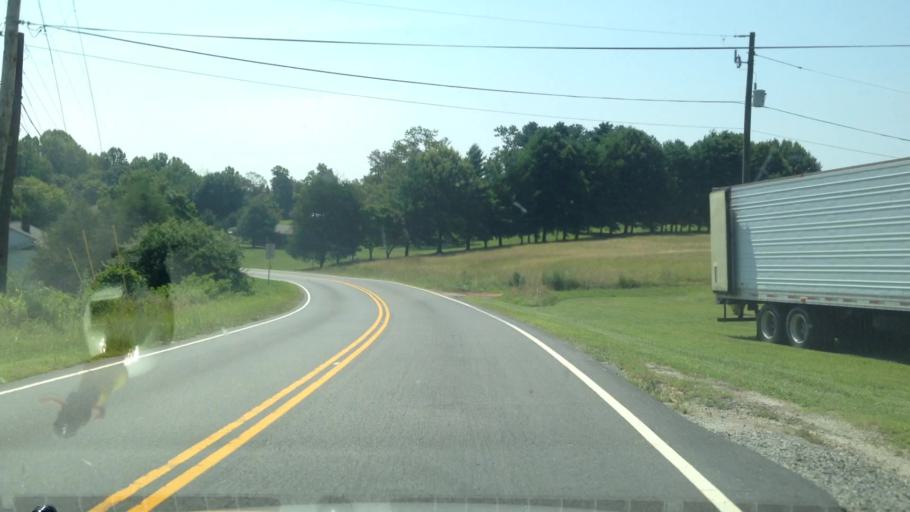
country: US
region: Virginia
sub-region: Patrick County
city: Stuart
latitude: 36.5819
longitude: -80.2777
